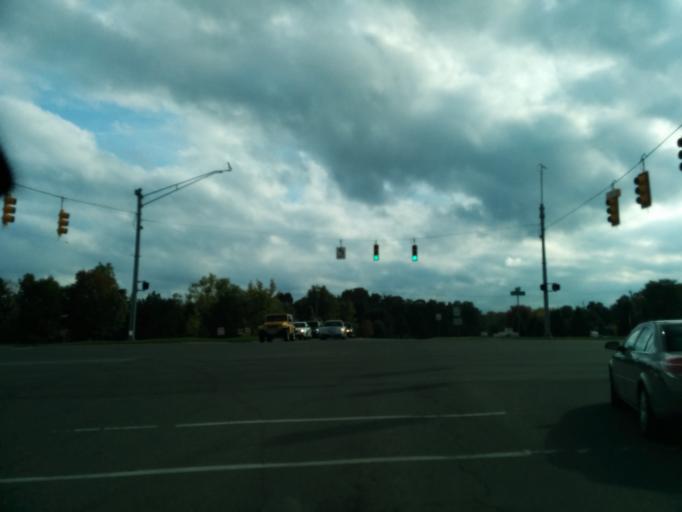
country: US
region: Michigan
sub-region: Oakland County
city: Waterford
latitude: 42.6499
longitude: -83.4934
